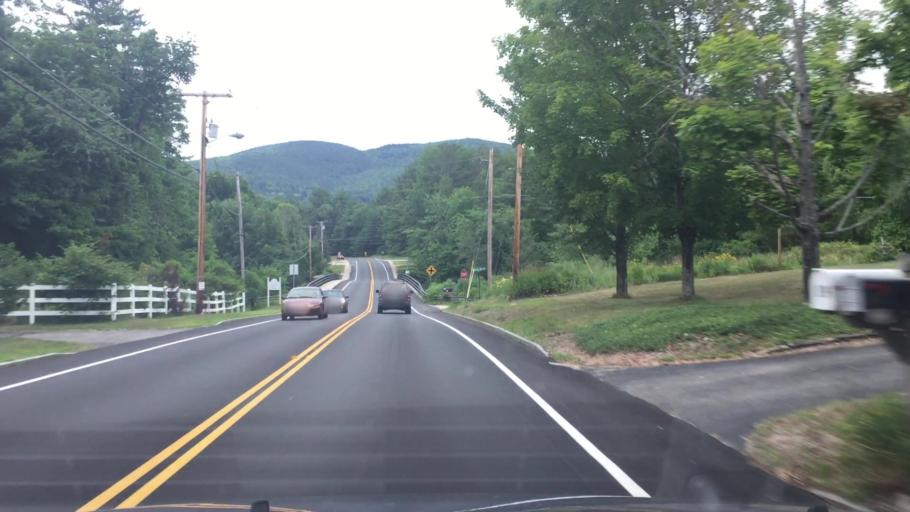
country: US
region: New Hampshire
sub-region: Carroll County
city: Freedom
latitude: 43.7973
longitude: -71.0568
